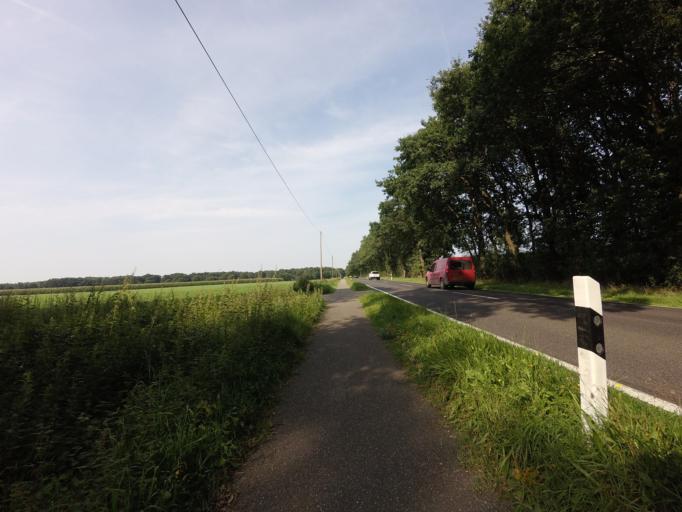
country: DE
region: Lower Saxony
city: Getelo
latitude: 52.4621
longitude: 6.8377
